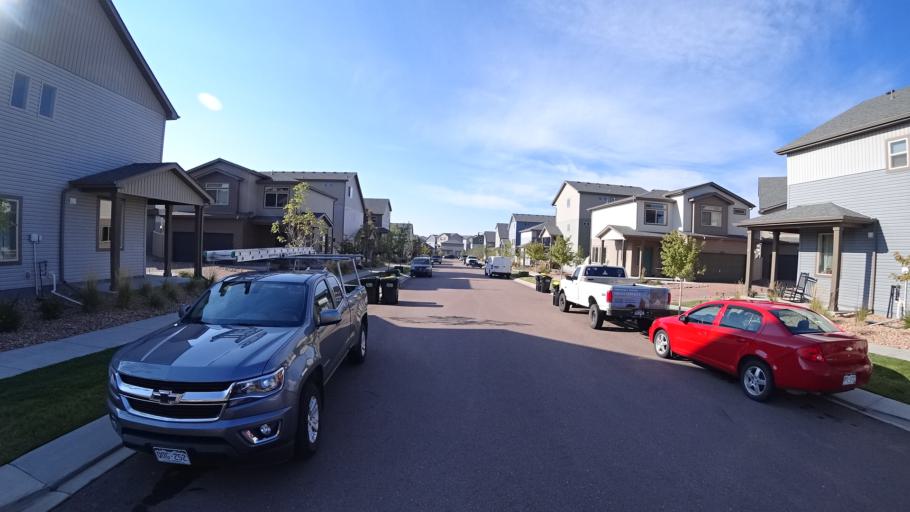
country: US
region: Colorado
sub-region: El Paso County
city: Cimarron Hills
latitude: 38.9293
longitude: -104.6606
